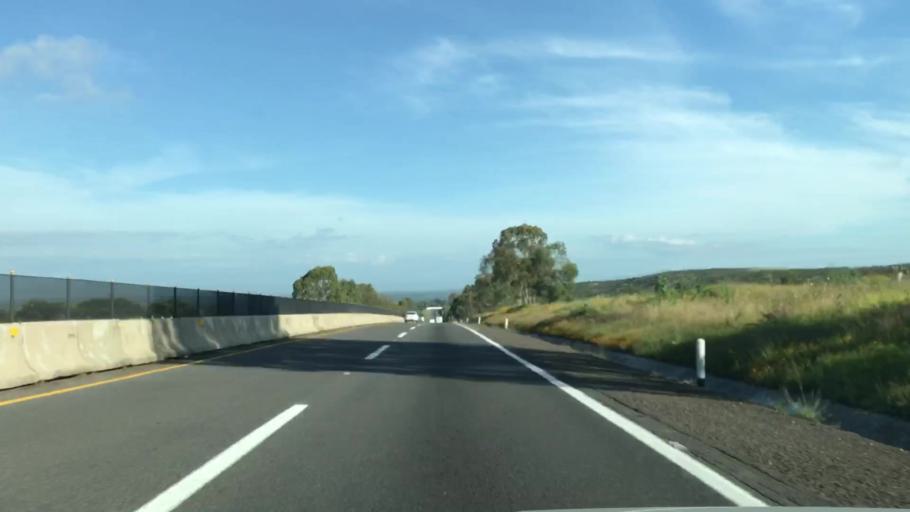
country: MX
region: Jalisco
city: Encarnacion de Diaz
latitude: 21.3868
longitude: -102.1424
